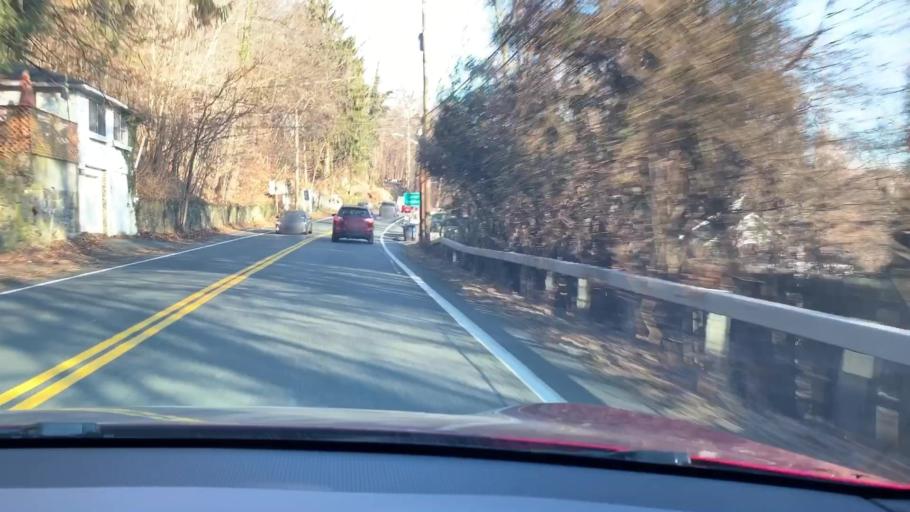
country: US
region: New York
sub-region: Rockland County
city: Piermont
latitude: 41.0508
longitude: -73.9225
